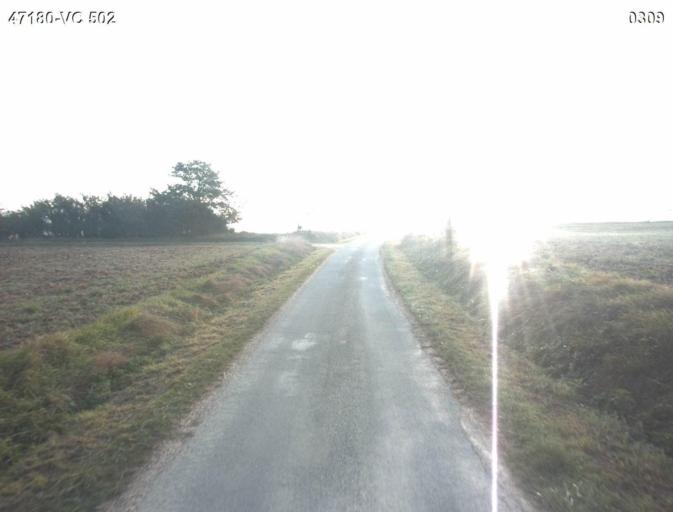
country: FR
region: Aquitaine
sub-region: Departement du Lot-et-Garonne
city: Sainte-Colombe-en-Bruilhois
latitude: 44.1625
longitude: 0.4785
